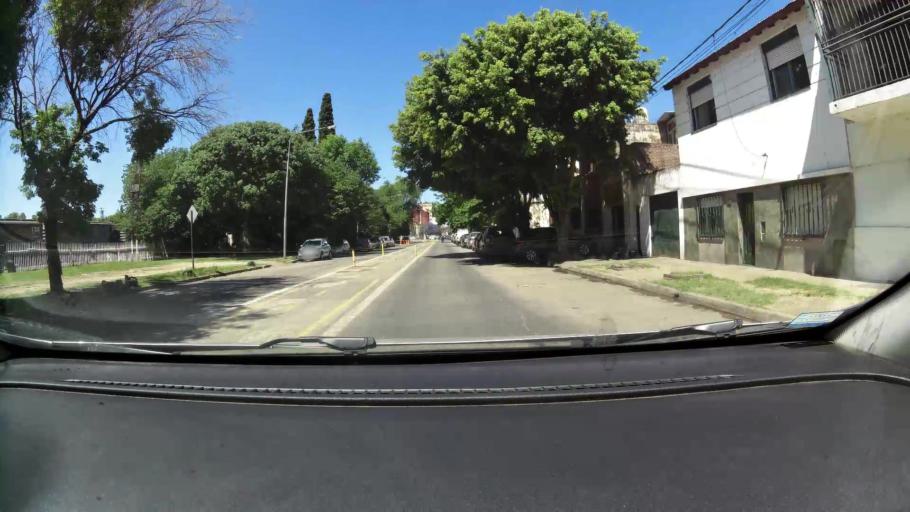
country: AR
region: Santa Fe
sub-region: Departamento de Rosario
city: Rosario
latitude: -32.9335
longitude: -60.6733
